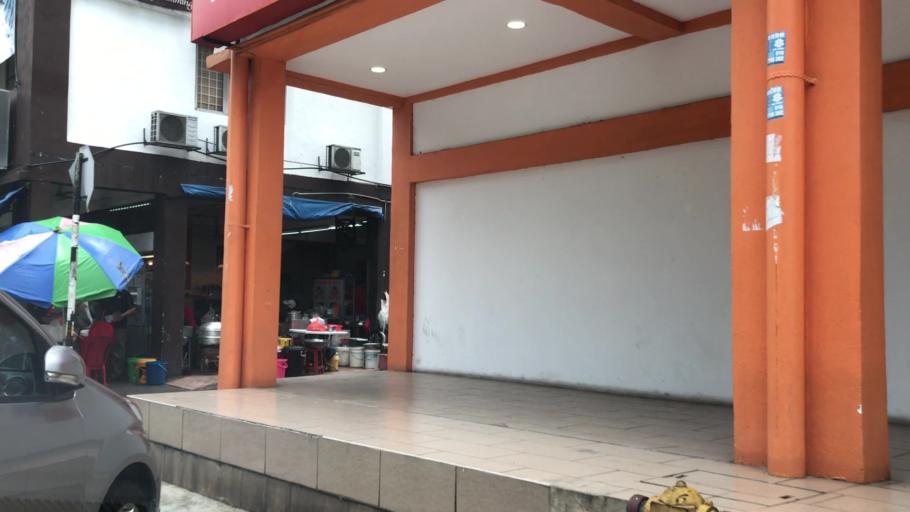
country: MY
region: Selangor
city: Subang Jaya
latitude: 3.0465
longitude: 101.6222
